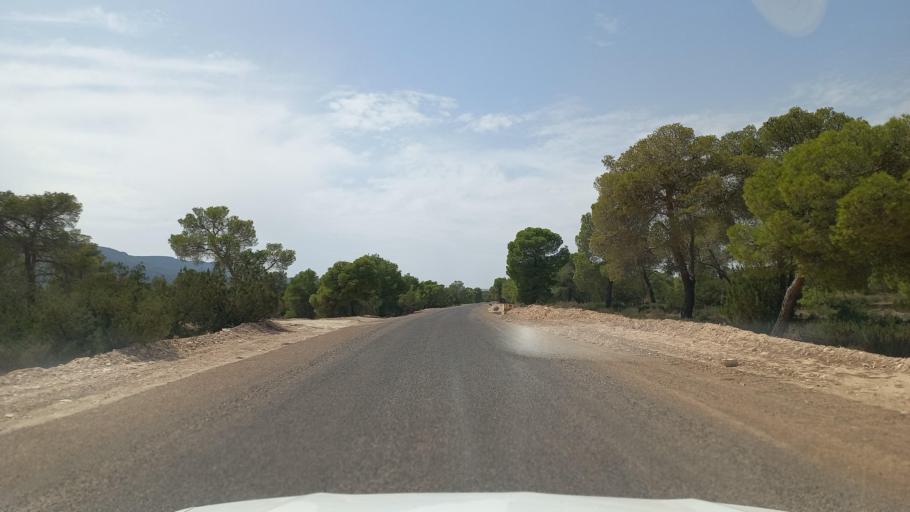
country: TN
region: Al Qasrayn
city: Sbiba
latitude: 35.3814
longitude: 8.9261
